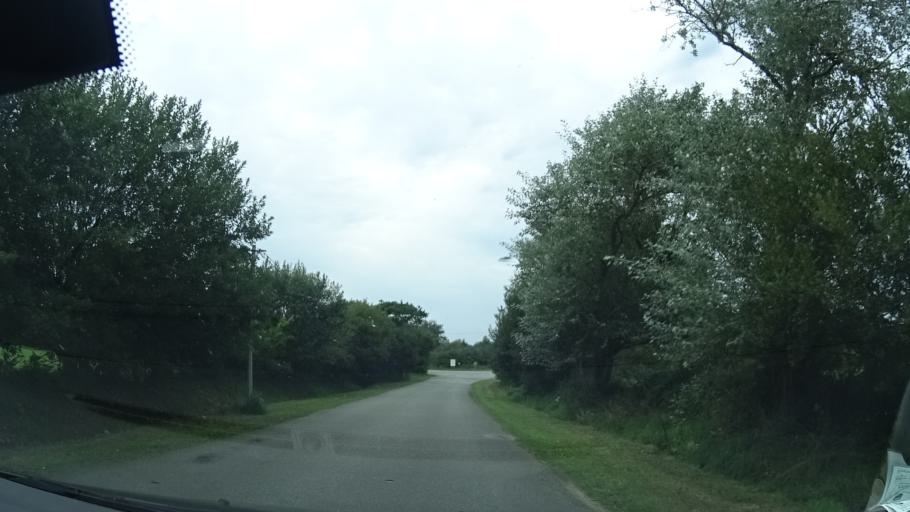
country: FR
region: Brittany
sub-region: Departement du Finistere
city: Plouarzel
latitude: 48.4377
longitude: -4.7320
